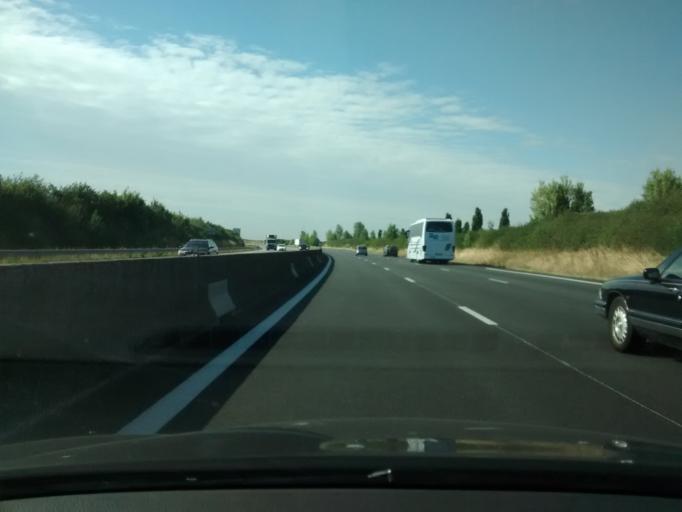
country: FR
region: Ile-de-France
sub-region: Departement des Yvelines
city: Sonchamp
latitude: 48.5372
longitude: 1.9041
